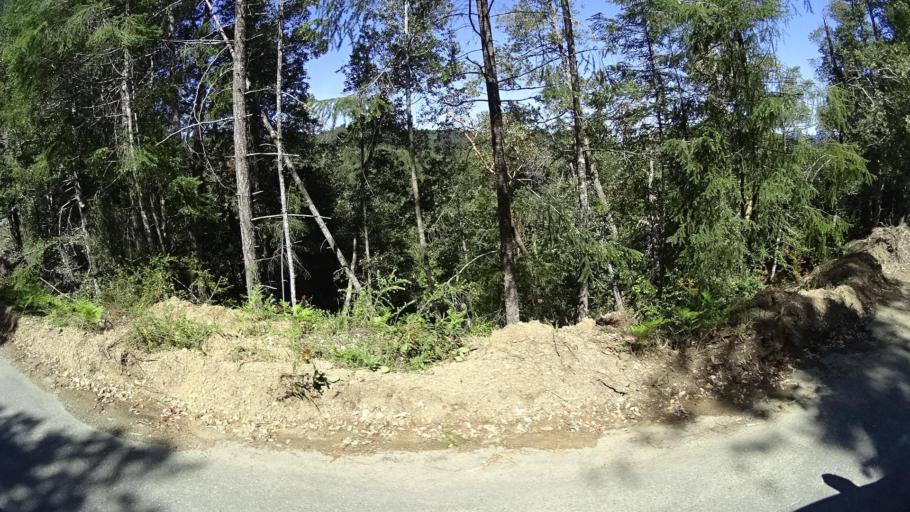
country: US
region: California
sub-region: Humboldt County
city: Redway
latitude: 40.1516
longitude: -124.0587
